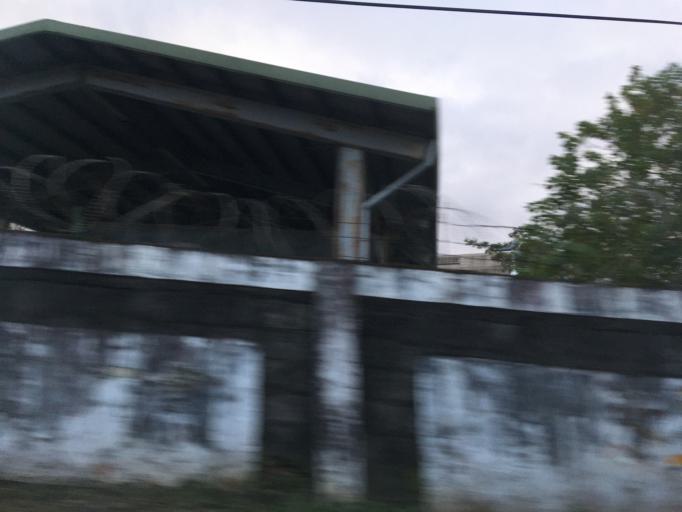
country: TW
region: Taiwan
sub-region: Yilan
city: Yilan
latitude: 24.7570
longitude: 121.7397
